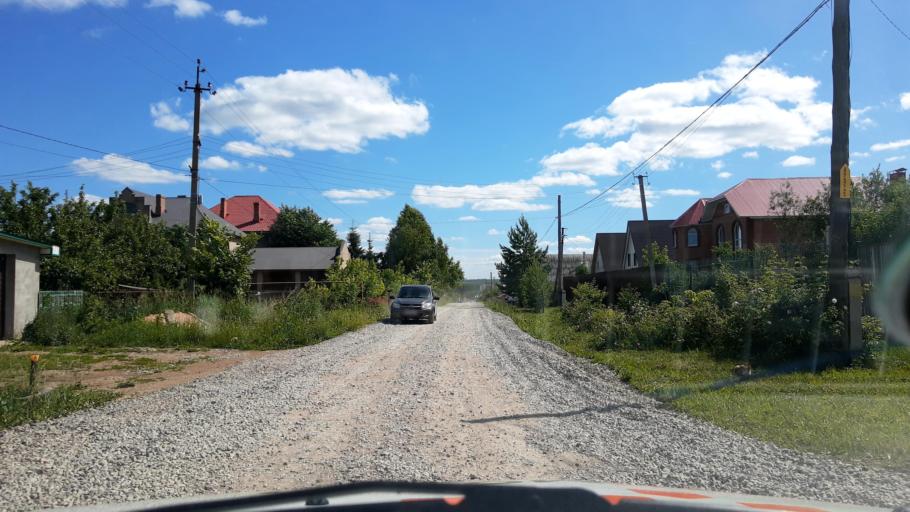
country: RU
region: Bashkortostan
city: Iglino
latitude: 54.8491
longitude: 56.4231
